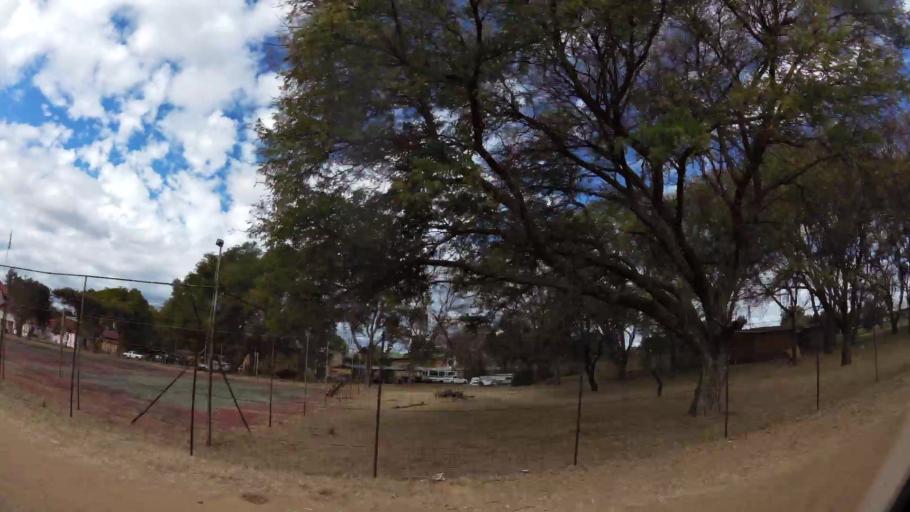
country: ZA
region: Limpopo
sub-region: Waterberg District Municipality
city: Modimolle
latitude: -24.7044
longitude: 28.4005
